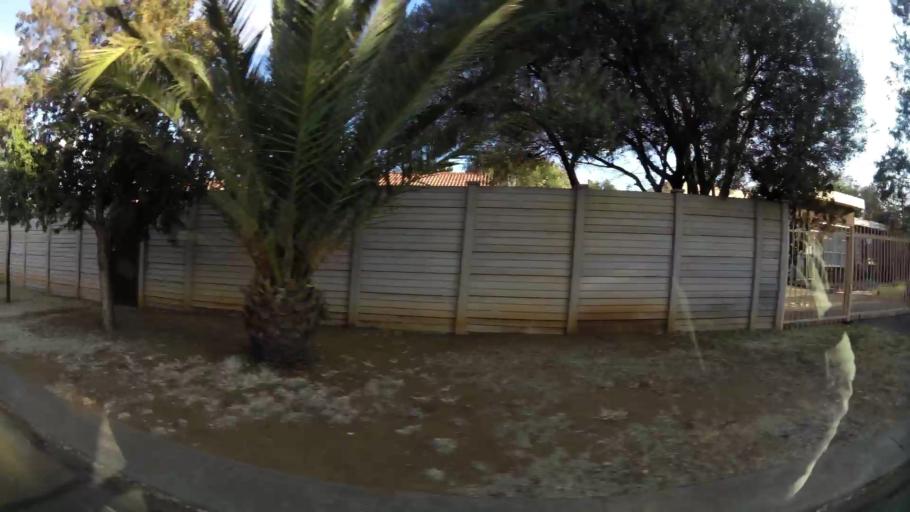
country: ZA
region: Orange Free State
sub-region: Mangaung Metropolitan Municipality
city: Bloemfontein
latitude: -29.1543
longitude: 26.1817
